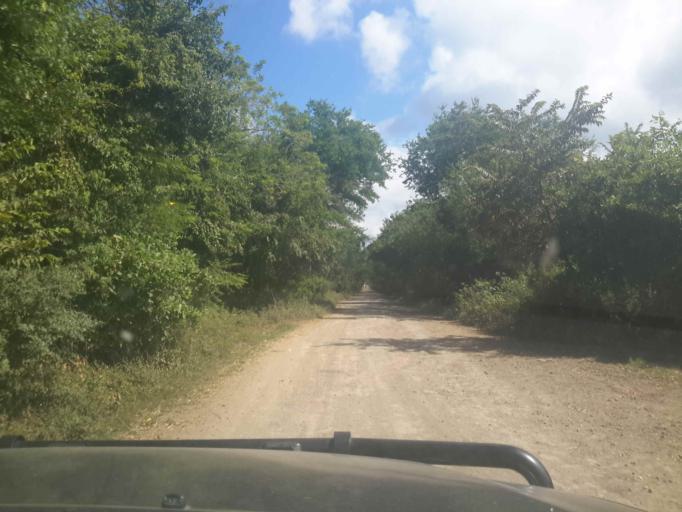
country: NI
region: Granada
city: Nandaime
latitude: 11.6671
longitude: -85.9445
